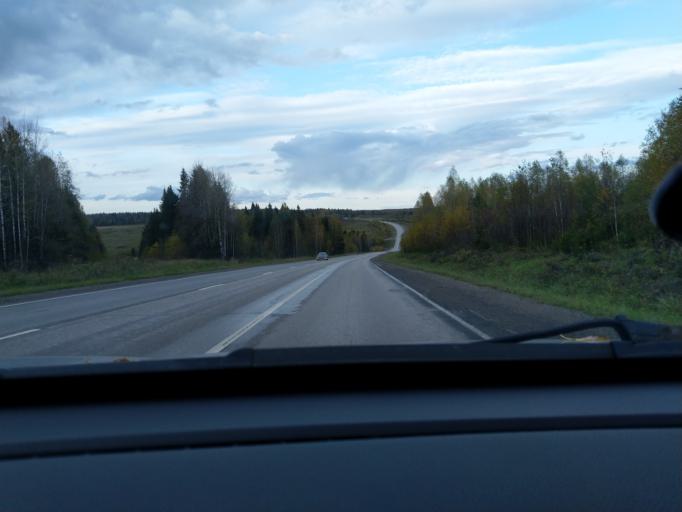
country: RU
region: Perm
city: Dobryanka
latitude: 58.4254
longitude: 56.5286
